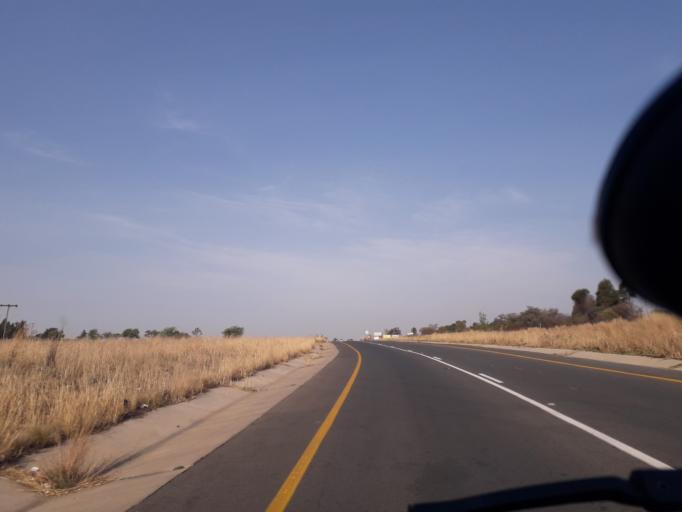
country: ZA
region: Gauteng
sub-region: West Rand District Municipality
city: Muldersdriseloop
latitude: -25.9699
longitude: 27.9087
